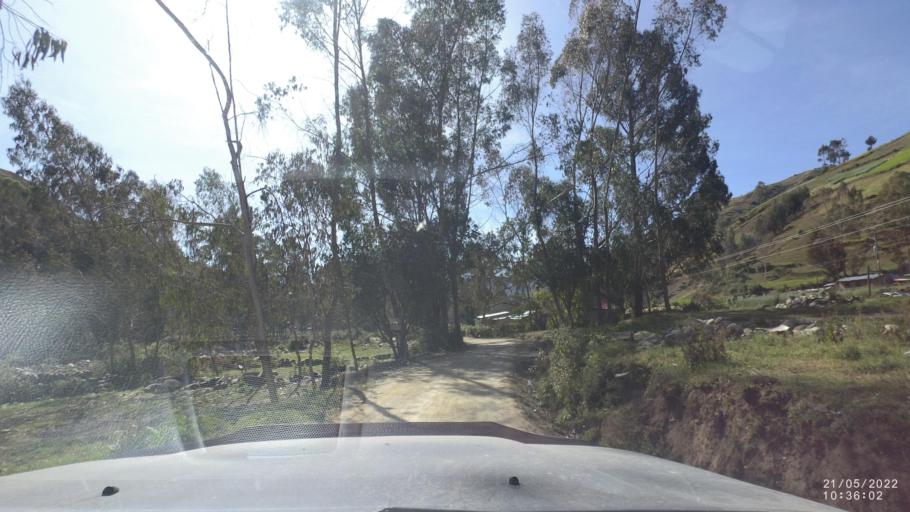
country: BO
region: Cochabamba
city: Colomi
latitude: -17.3157
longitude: -65.9250
